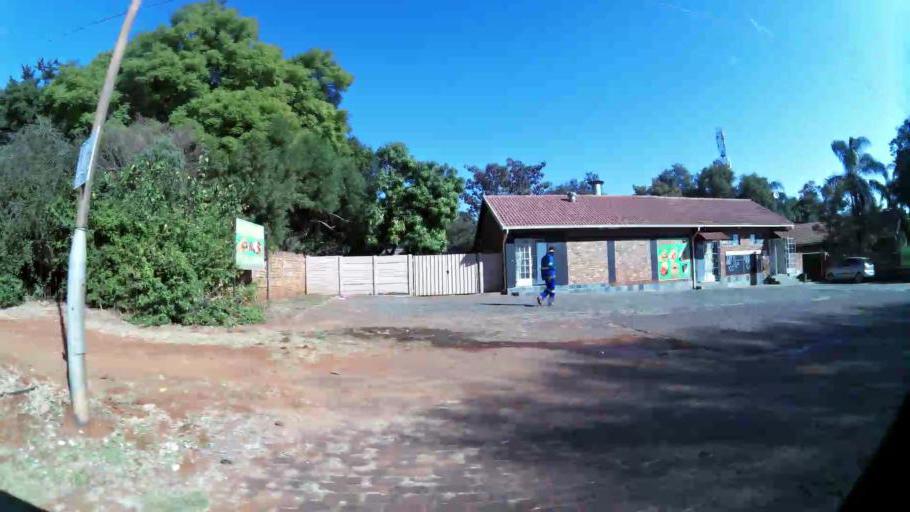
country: ZA
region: Gauteng
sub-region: City of Tshwane Metropolitan Municipality
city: Pretoria
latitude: -25.6809
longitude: 28.1340
